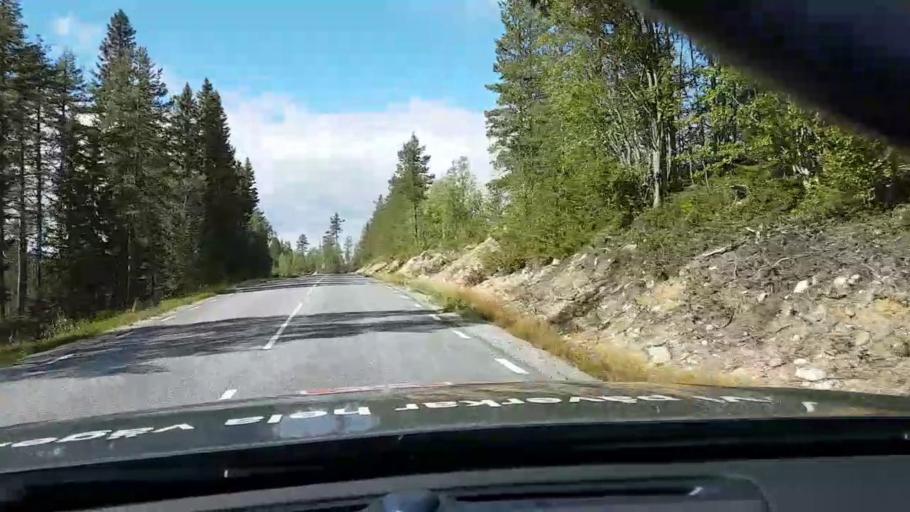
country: SE
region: Vaesterbotten
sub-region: Asele Kommun
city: Asele
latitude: 63.8327
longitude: 17.4504
